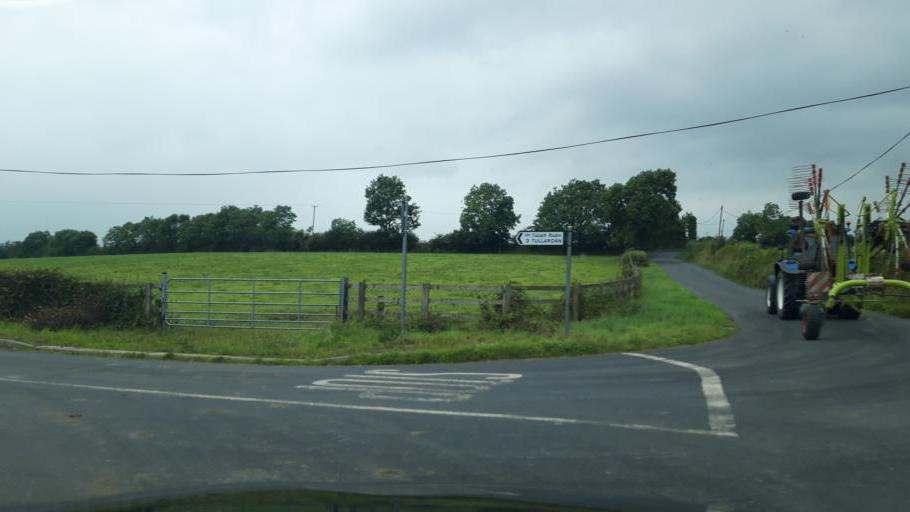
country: IE
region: Leinster
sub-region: Kilkenny
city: Ballyragget
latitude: 52.6871
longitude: -7.4290
